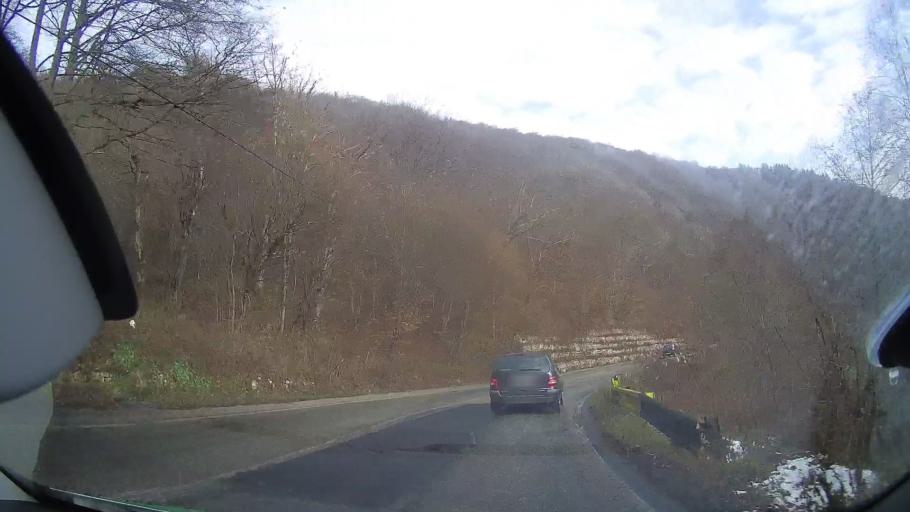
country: RO
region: Alba
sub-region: Oras Baia de Aries
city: Baia de Aries
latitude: 46.3819
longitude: 23.2579
